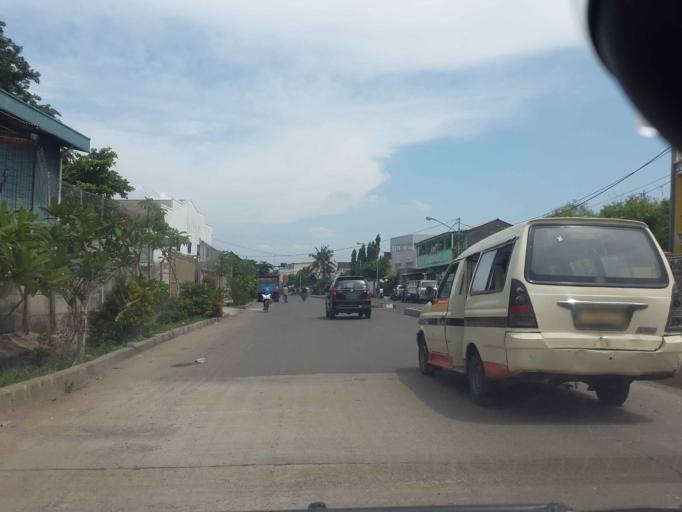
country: ID
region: Banten
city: Tangerang
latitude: -6.1550
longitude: 106.6613
